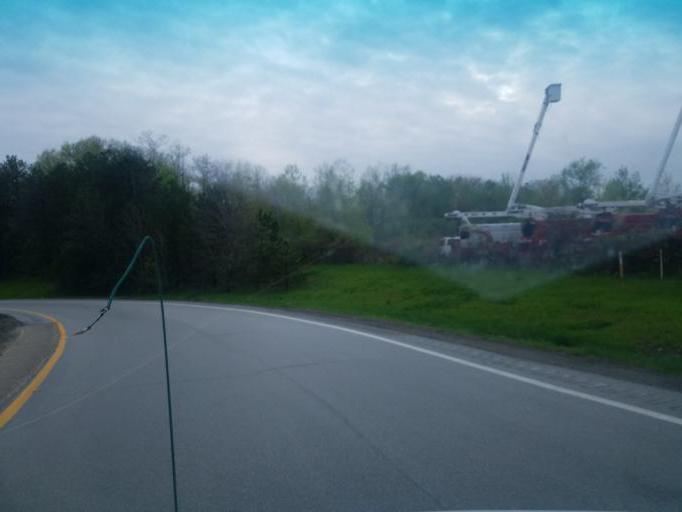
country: US
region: Ohio
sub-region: Ashtabula County
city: Geneva
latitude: 41.7879
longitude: -80.8552
